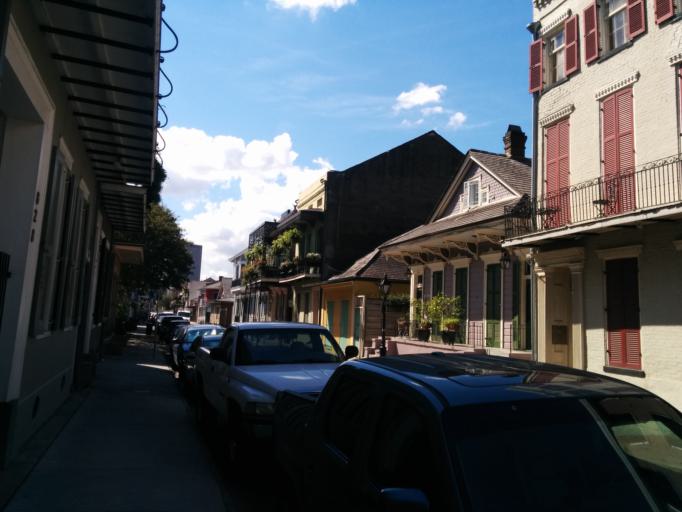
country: US
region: Louisiana
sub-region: Orleans Parish
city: New Orleans
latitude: 29.9612
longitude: -90.0661
